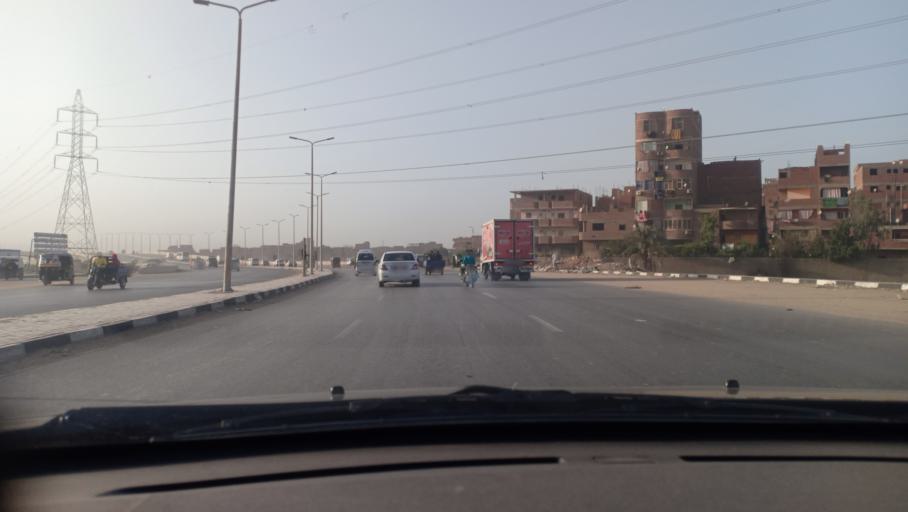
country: EG
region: Muhafazat al Qalyubiyah
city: Qalyub
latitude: 30.1403
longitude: 31.2642
